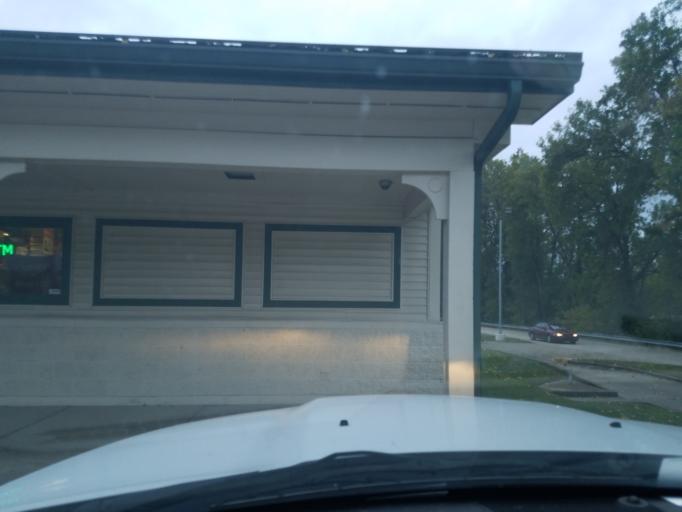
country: US
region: Indiana
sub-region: Vanderburgh County
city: Evansville
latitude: 37.9147
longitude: -87.5492
